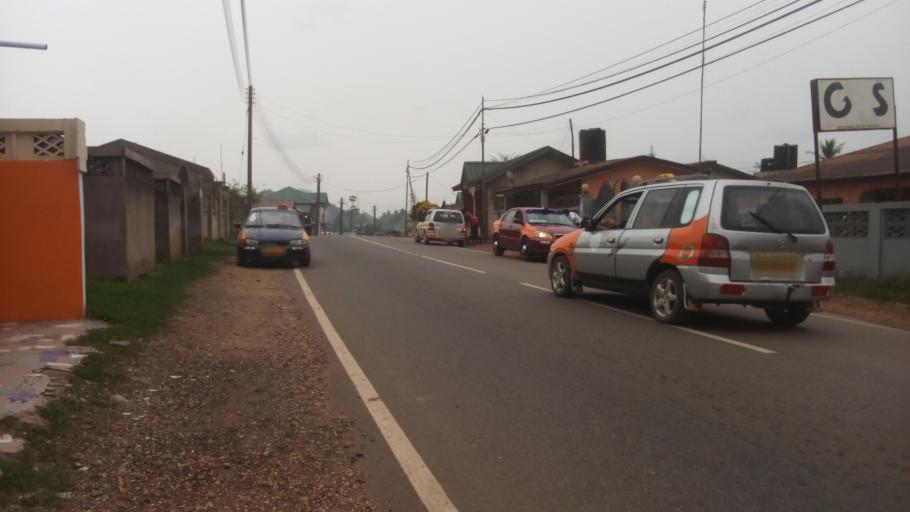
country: GH
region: Western
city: Tarkwa
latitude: 5.2853
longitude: -2.0007
